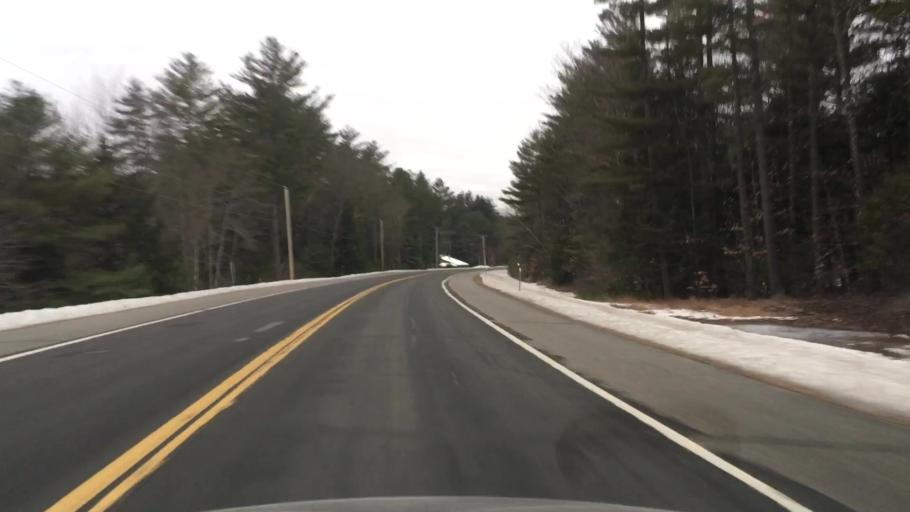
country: US
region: New Hampshire
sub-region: Merrimack County
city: Henniker
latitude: 43.2105
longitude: -71.8632
